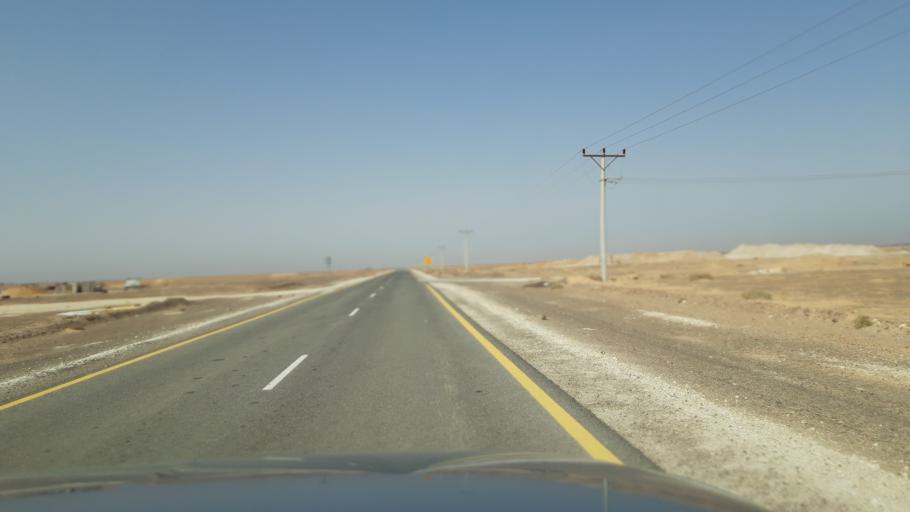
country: JO
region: Amman
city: Al Azraq ash Shamali
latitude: 31.7796
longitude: 36.7865
